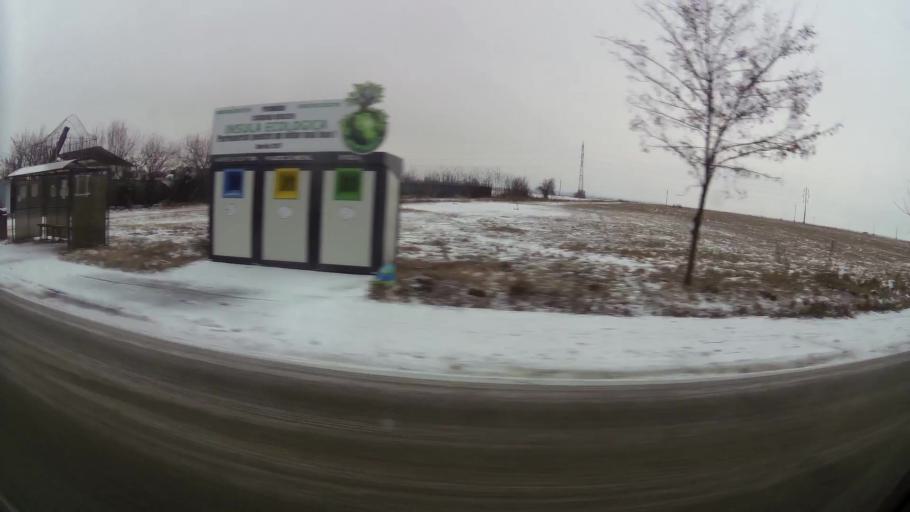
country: RO
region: Prahova
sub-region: Comuna Berceni
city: Corlatesti
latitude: 44.9263
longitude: 26.0695
